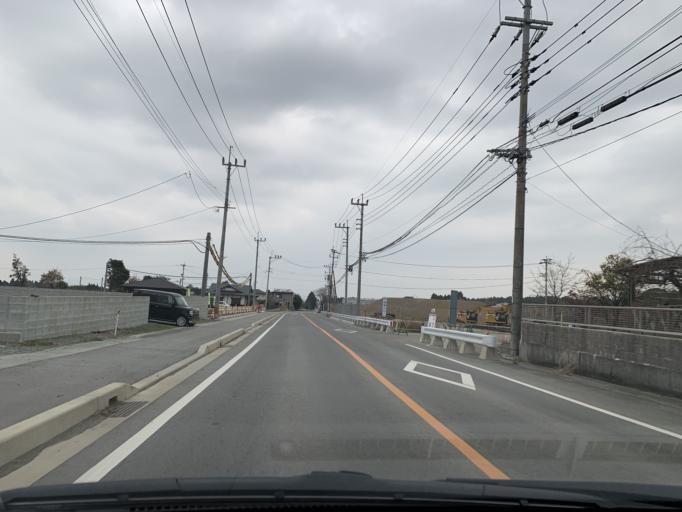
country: JP
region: Kumamoto
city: Ozu
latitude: 32.8901
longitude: 130.8970
